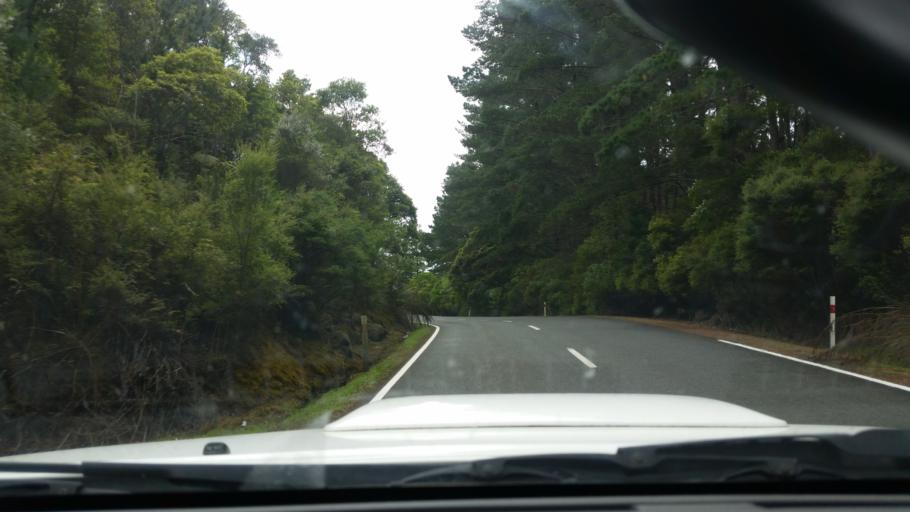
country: NZ
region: Northland
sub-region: Kaipara District
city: Dargaville
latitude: -35.7321
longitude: 173.8632
